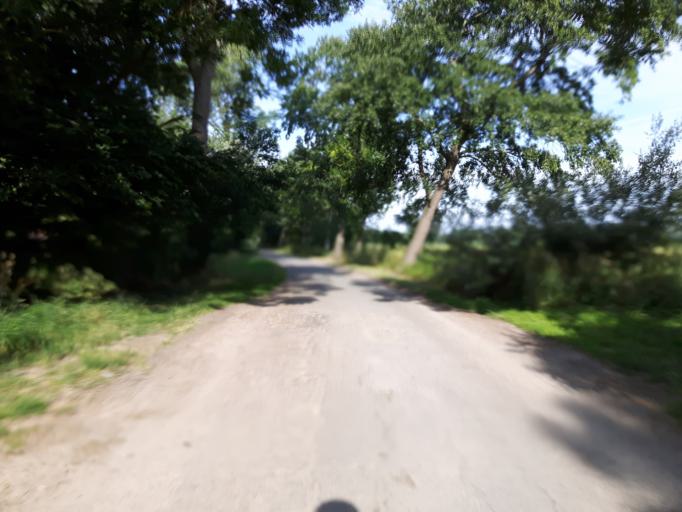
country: DE
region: Lower Saxony
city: Lemwerder
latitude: 53.1490
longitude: 8.5578
